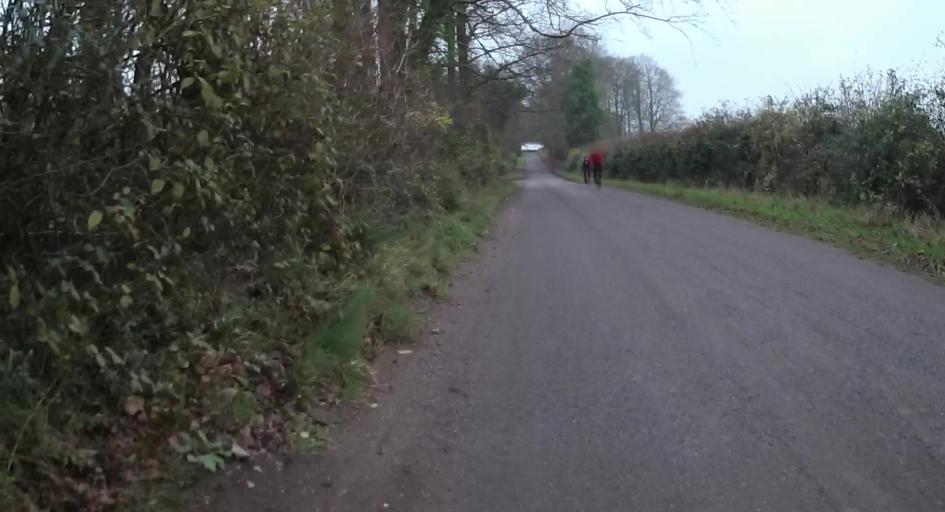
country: GB
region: England
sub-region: Hampshire
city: Kings Worthy
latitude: 51.1280
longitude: -1.2114
